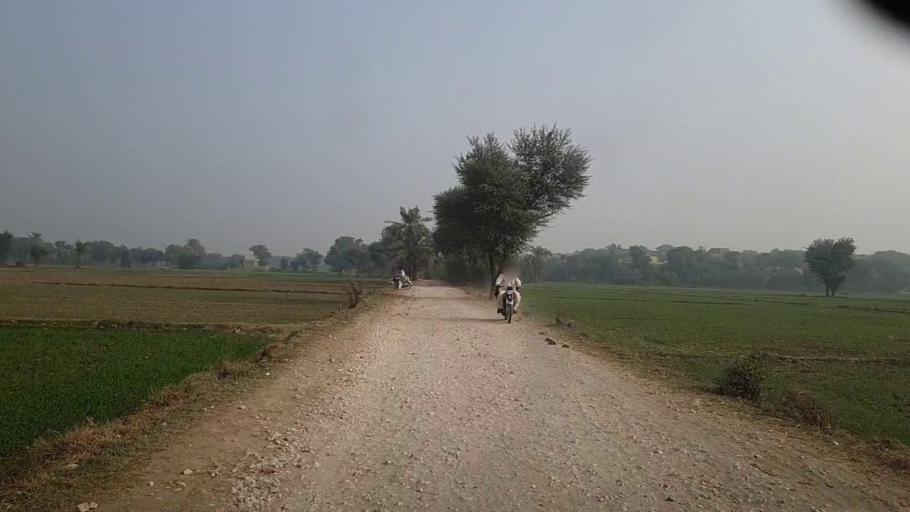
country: PK
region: Sindh
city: Bozdar
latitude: 27.1337
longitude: 68.6559
